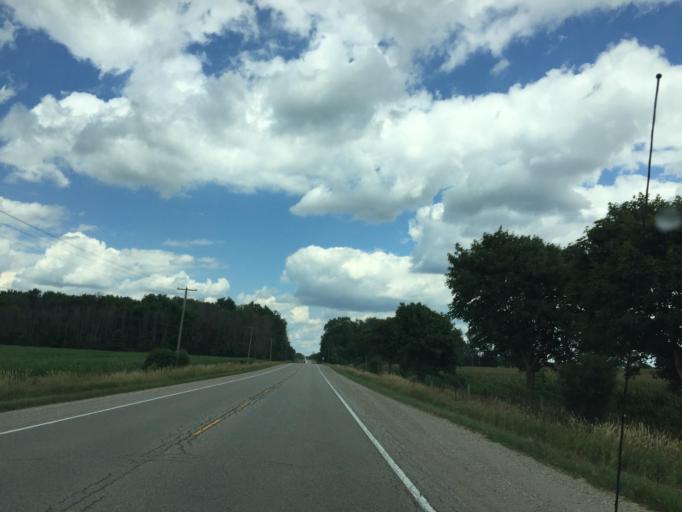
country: CA
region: Ontario
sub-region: Wellington County
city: Guelph
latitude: 43.5481
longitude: -80.3512
